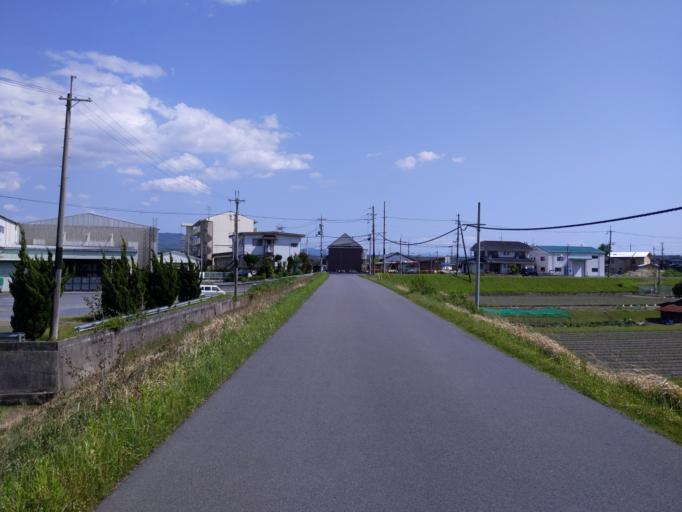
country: JP
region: Nara
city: Nara-shi
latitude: 34.7409
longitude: 135.8044
